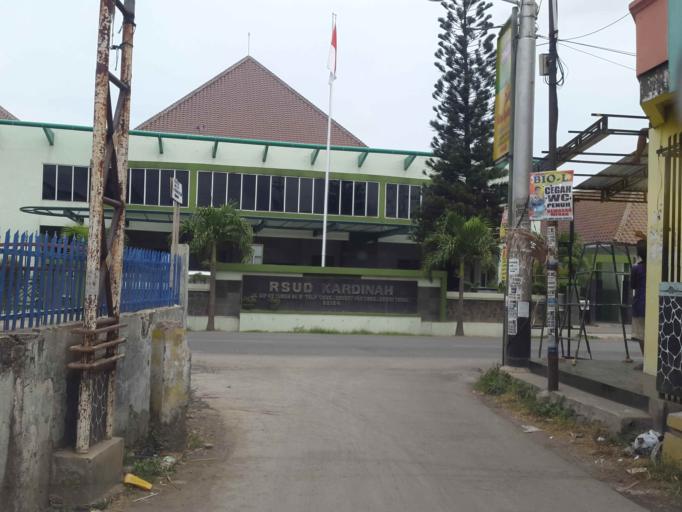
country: ID
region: Central Java
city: Tegal
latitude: -6.8859
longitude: 109.1349
